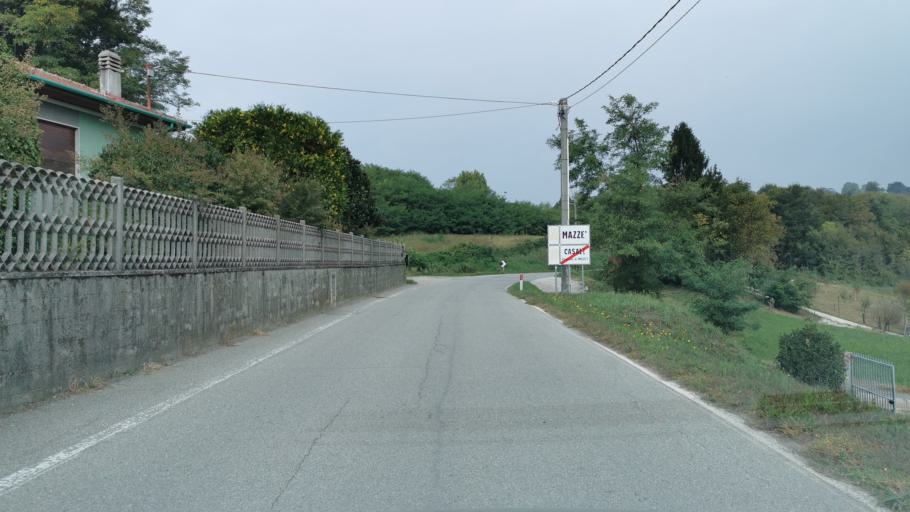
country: IT
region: Piedmont
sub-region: Provincia di Torino
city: Tonengo-Casale
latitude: 45.2945
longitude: 7.9420
